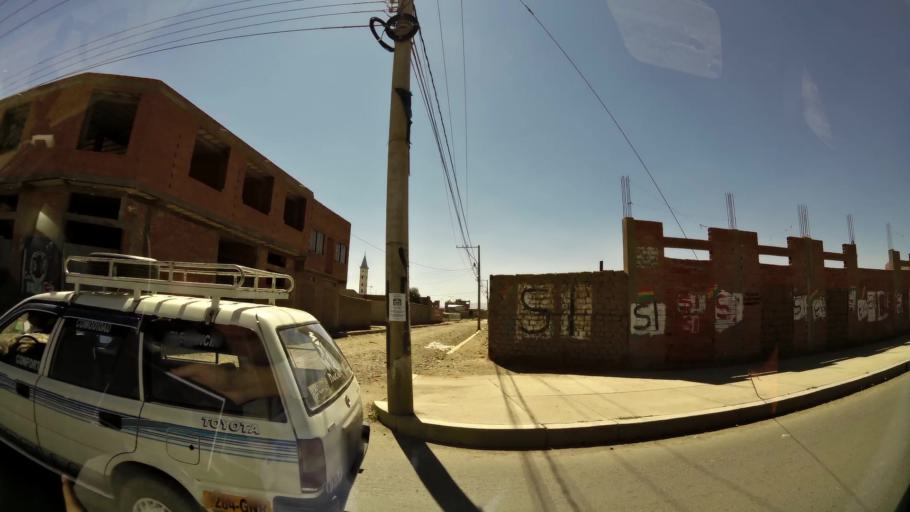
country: BO
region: La Paz
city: La Paz
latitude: -16.5206
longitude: -68.2213
